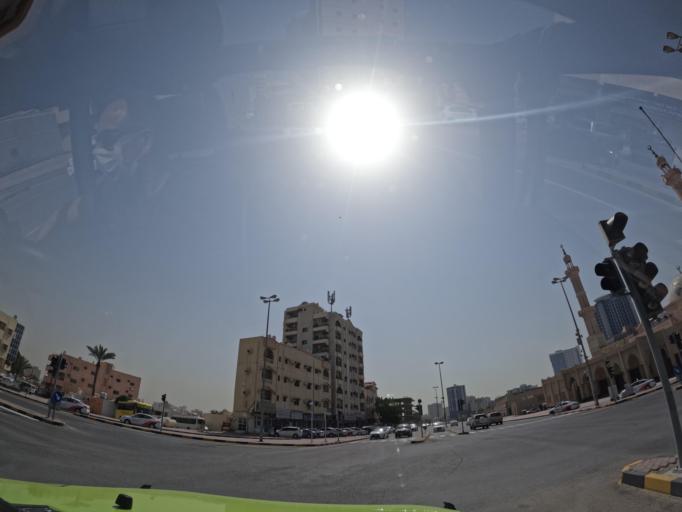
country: AE
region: Ajman
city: Ajman
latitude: 25.4151
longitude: 55.4467
